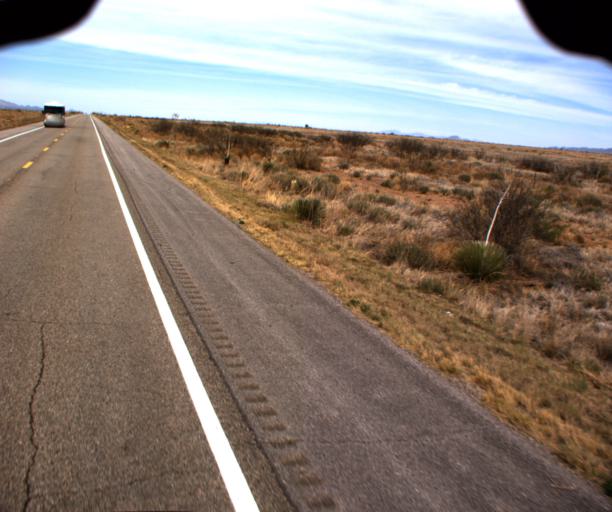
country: US
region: Arizona
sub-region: Cochise County
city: Pirtleville
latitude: 31.5322
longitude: -109.6523
